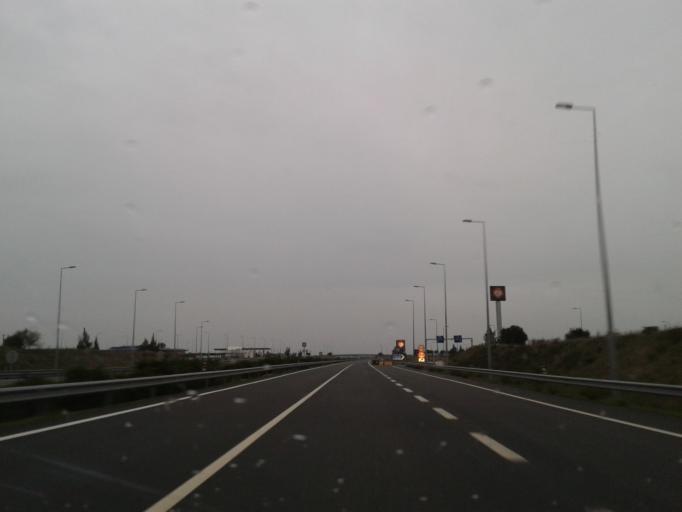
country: PT
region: Beja
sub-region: Aljustrel
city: Aljustrel
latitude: 37.9206
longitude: -8.2425
